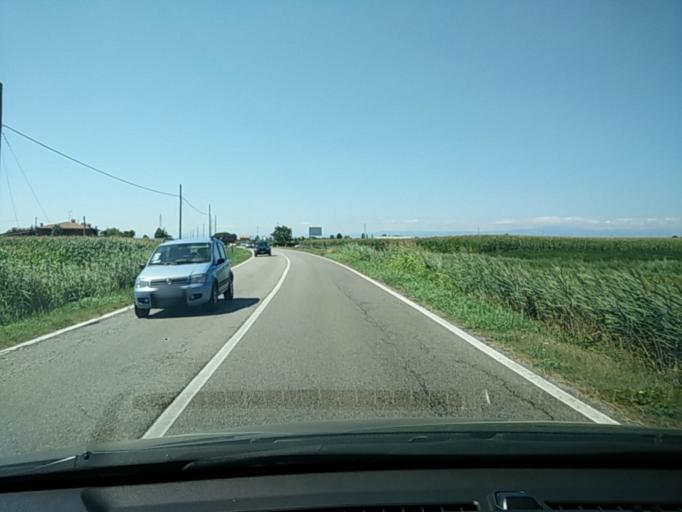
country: IT
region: Veneto
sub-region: Provincia di Venezia
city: Caorle
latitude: 45.6343
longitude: 12.8573
